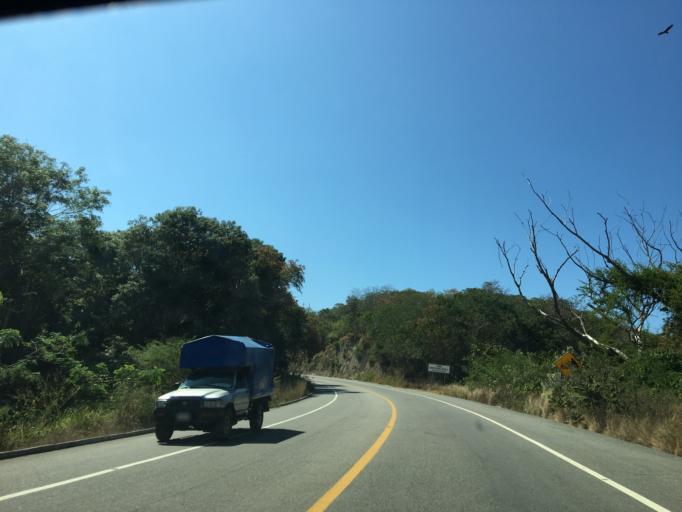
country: MX
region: Oaxaca
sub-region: Santa Maria Huatulco
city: Sector H Tres
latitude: 15.7813
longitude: -96.2106
